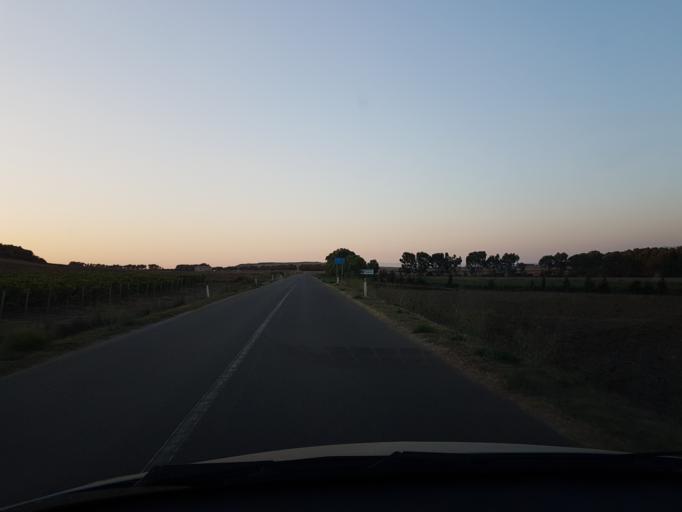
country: IT
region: Sardinia
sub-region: Provincia di Oristano
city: Cabras
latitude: 39.9640
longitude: 8.4536
